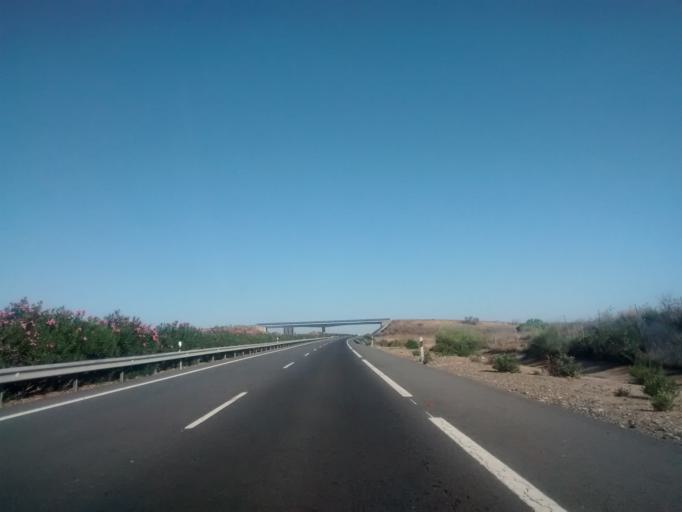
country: ES
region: Andalusia
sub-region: Provincia de Huelva
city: Huelva
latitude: 37.3314
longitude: -6.9155
